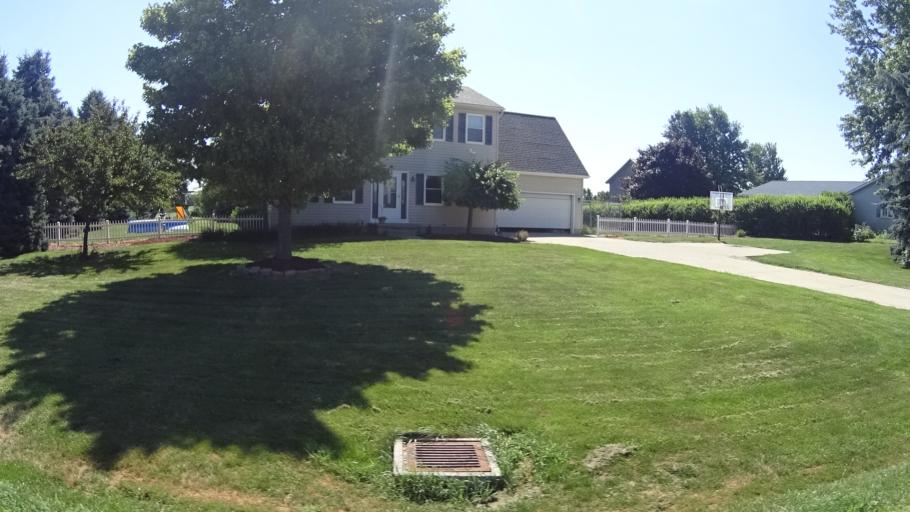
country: US
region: Ohio
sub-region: Erie County
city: Huron
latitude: 41.3592
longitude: -82.5746
